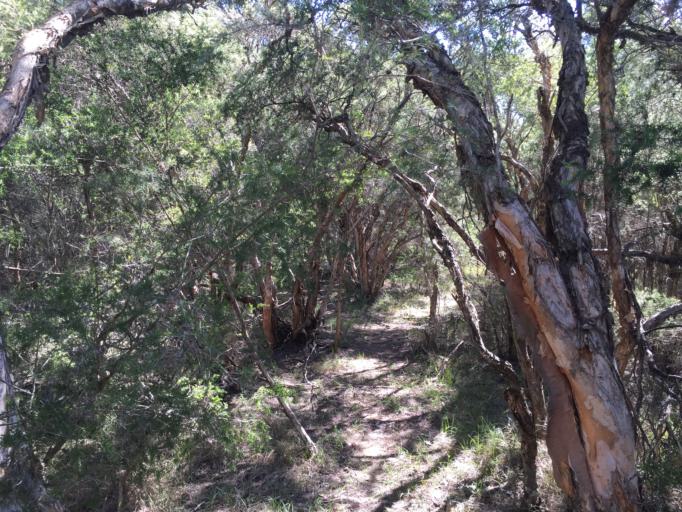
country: AU
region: New South Wales
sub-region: Blacktown
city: Stanhope Gardens
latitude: -33.7203
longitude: 150.9097
